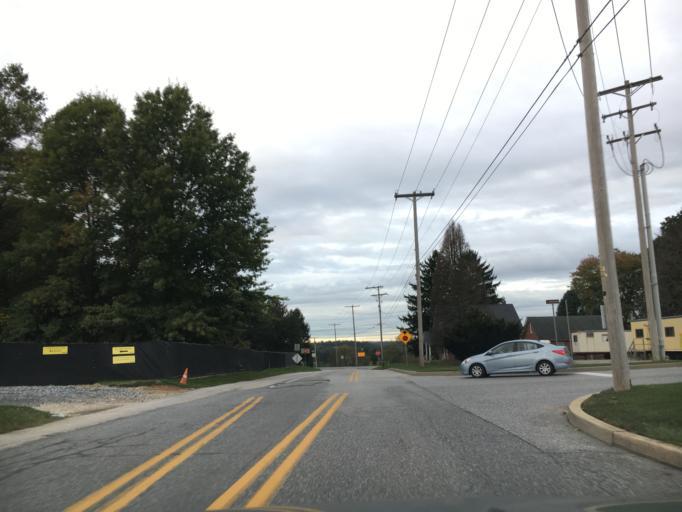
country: US
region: Pennsylvania
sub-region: York County
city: Grantley
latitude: 39.9231
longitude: -76.7174
